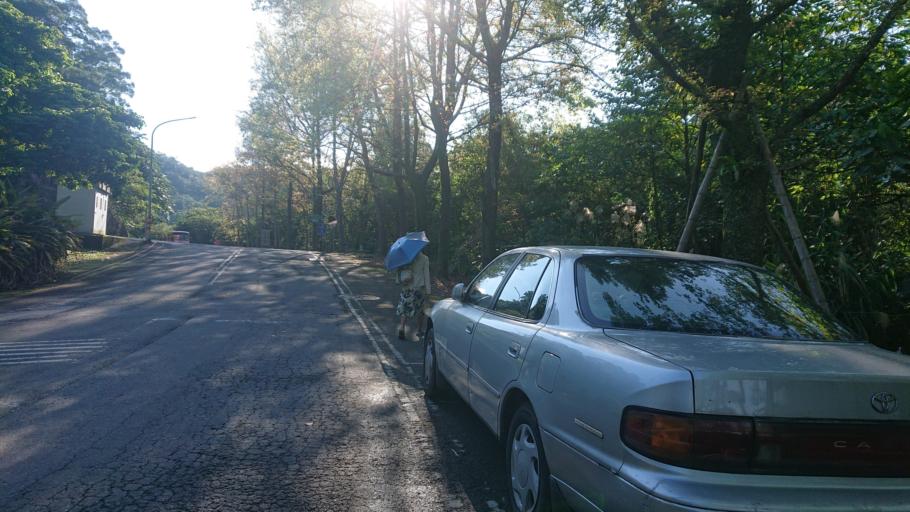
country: TW
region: Taipei
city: Taipei
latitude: 24.9787
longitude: 121.5691
